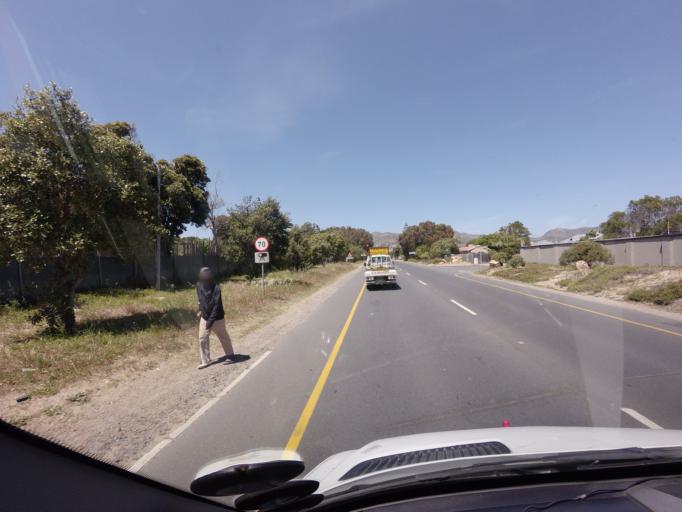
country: ZA
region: Western Cape
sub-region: City of Cape Town
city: Constantia
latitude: -34.1173
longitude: 18.3880
